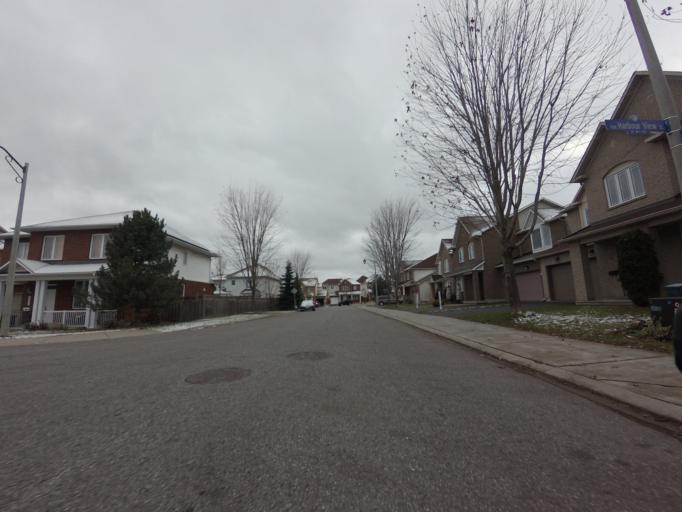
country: CA
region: Ontario
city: Bells Corners
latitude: 45.2678
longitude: -75.7086
